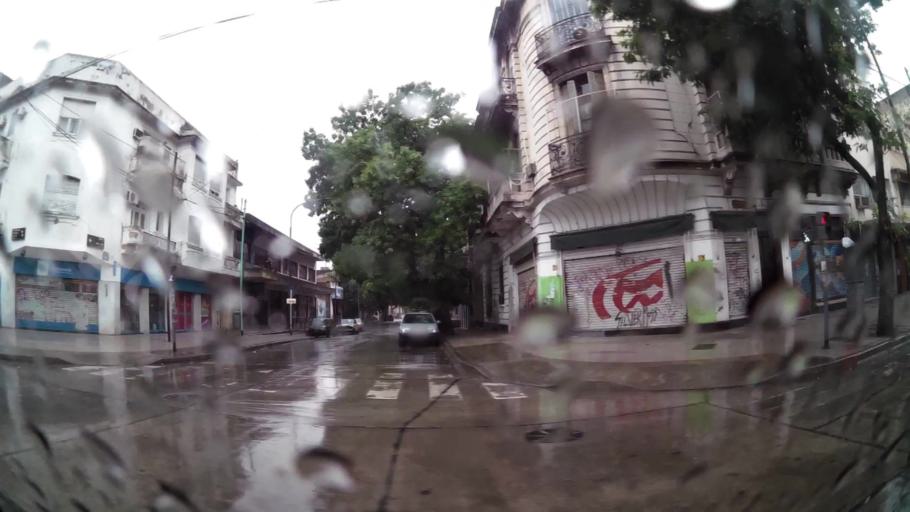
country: AR
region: Buenos Aires
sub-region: Partido de Avellaneda
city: Avellaneda
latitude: -34.6366
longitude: -58.3698
